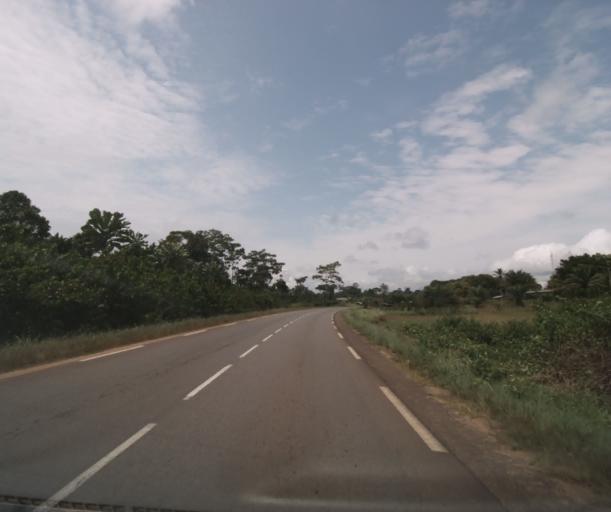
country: CM
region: South Province
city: Kribi
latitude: 3.0207
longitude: 9.9589
